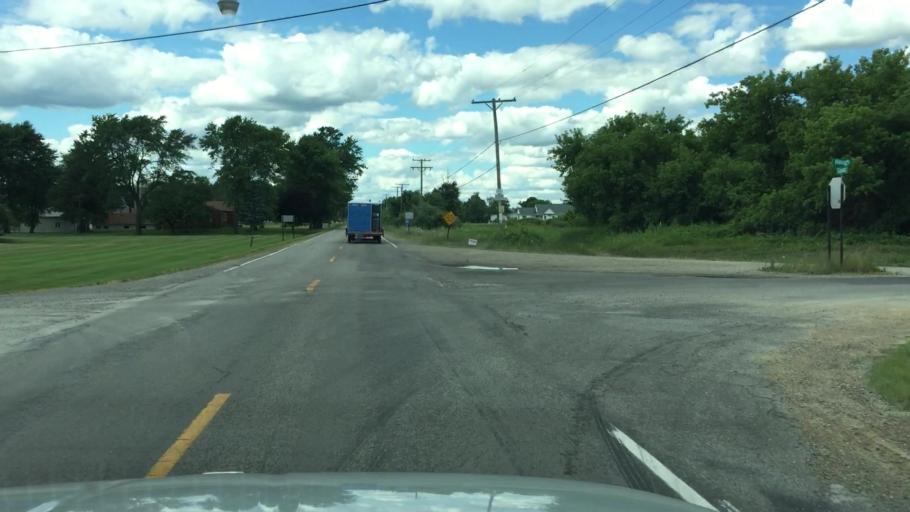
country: US
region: Michigan
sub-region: Macomb County
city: Armada
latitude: 42.9088
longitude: -82.9454
